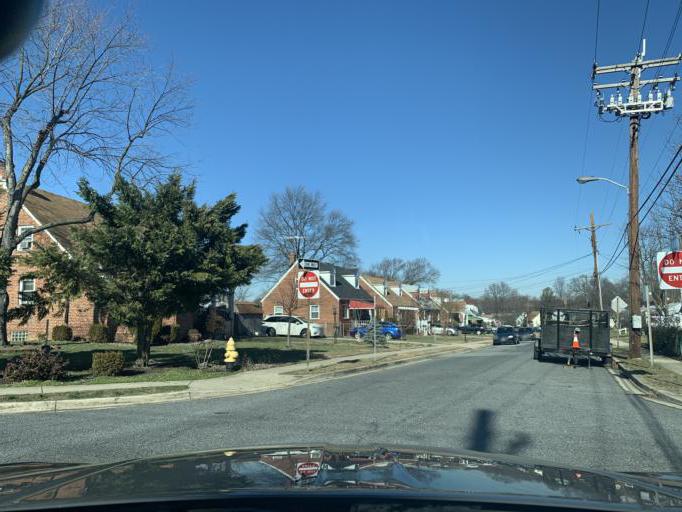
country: US
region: Maryland
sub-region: Anne Arundel County
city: Glen Burnie
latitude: 39.1622
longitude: -76.6170
